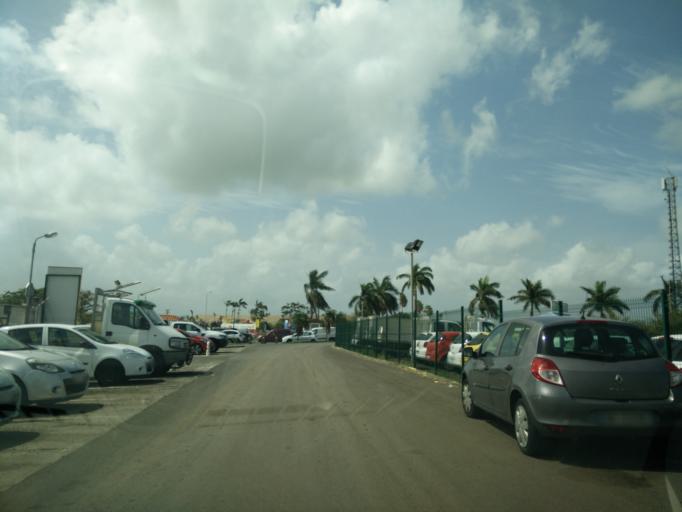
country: MQ
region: Martinique
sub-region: Martinique
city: Le Lamentin
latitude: 14.5991
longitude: -61.0020
